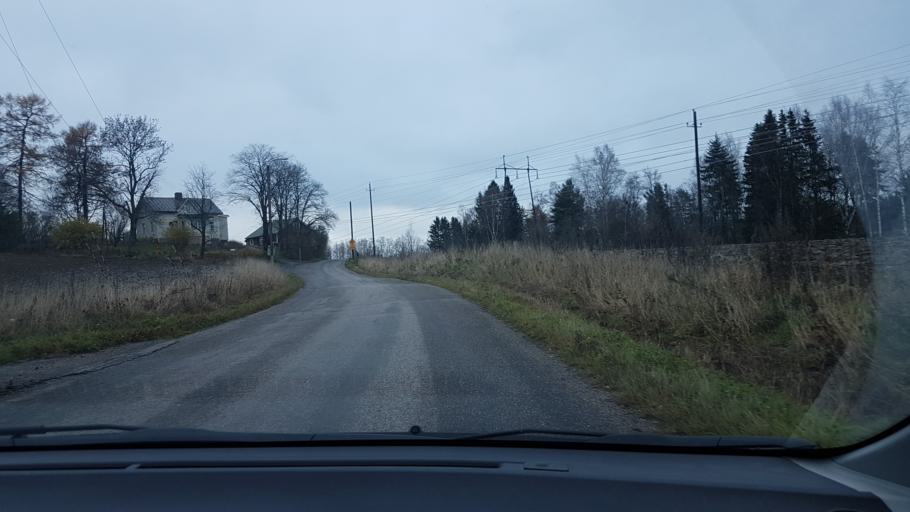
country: FI
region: Uusimaa
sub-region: Helsinki
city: Vantaa
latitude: 60.2815
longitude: 25.1387
